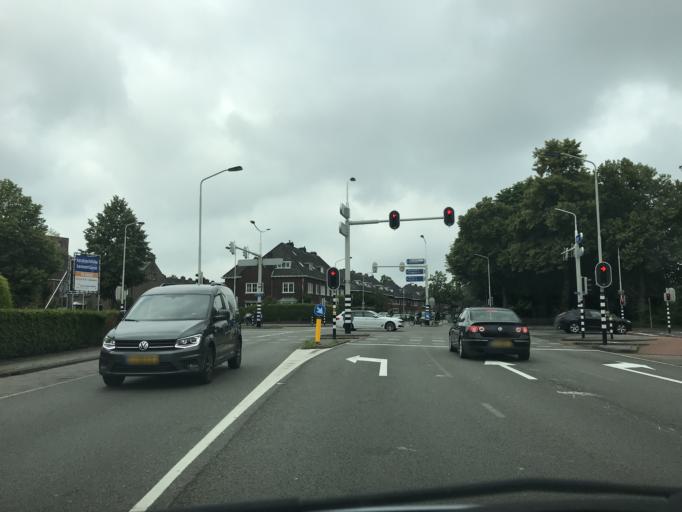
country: NL
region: North Brabant
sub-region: Gemeente Breda
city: Breda
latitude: 51.5788
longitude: 4.7710
